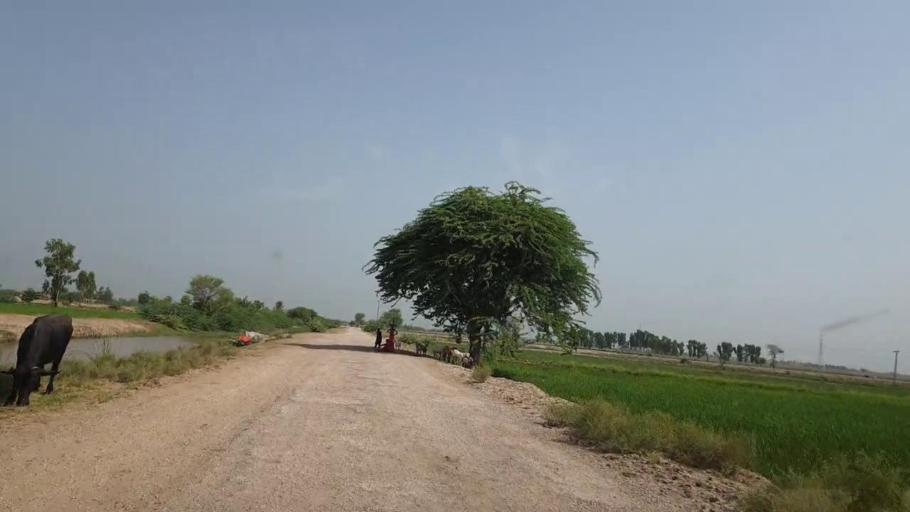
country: PK
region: Sindh
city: Lakhi
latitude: 27.8251
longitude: 68.6882
